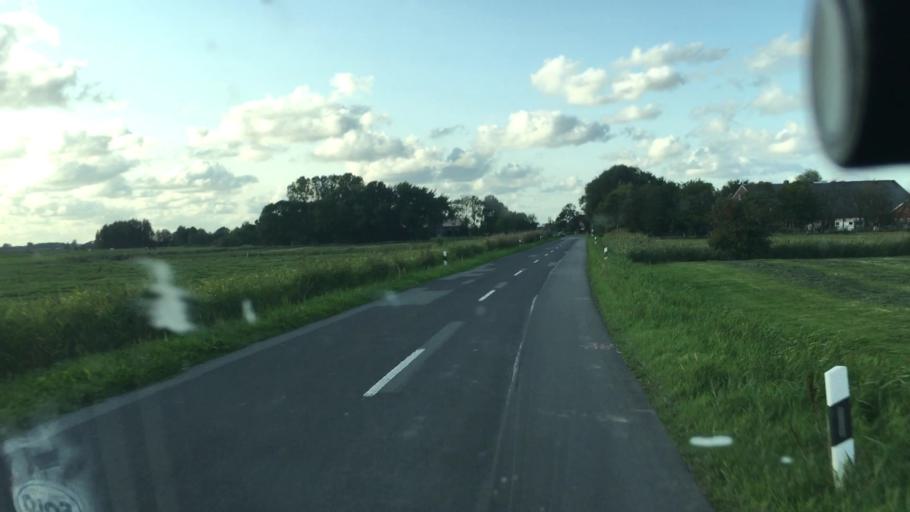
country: DE
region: Lower Saxony
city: Werdum
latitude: 53.6701
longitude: 7.7243
